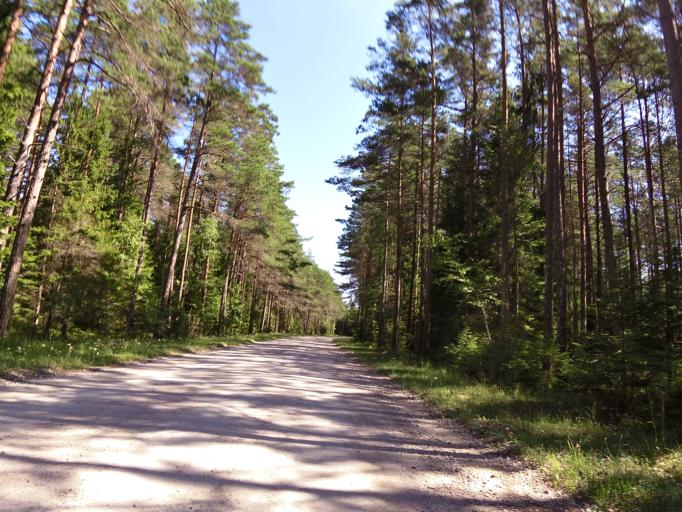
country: EE
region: Hiiumaa
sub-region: Kaerdla linn
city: Kardla
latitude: 58.9211
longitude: 22.3611
